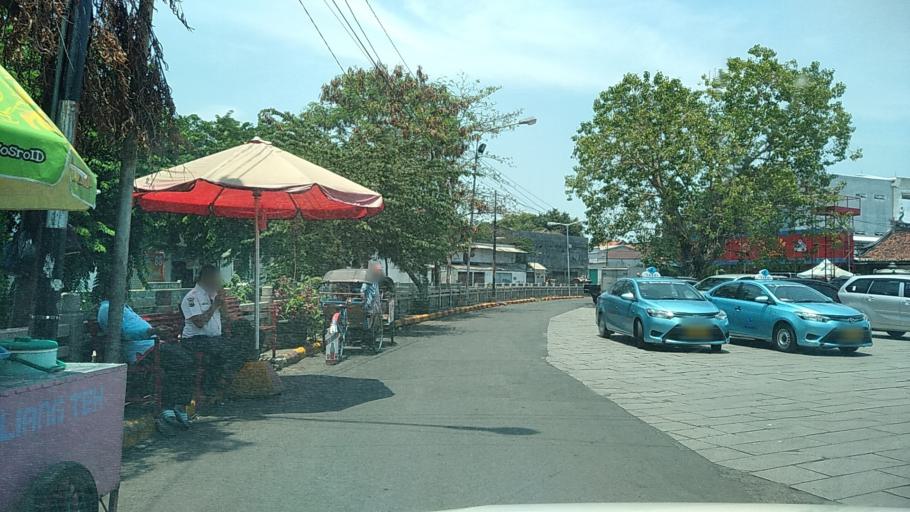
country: ID
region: Central Java
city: Semarang
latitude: -6.9744
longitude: 110.4279
